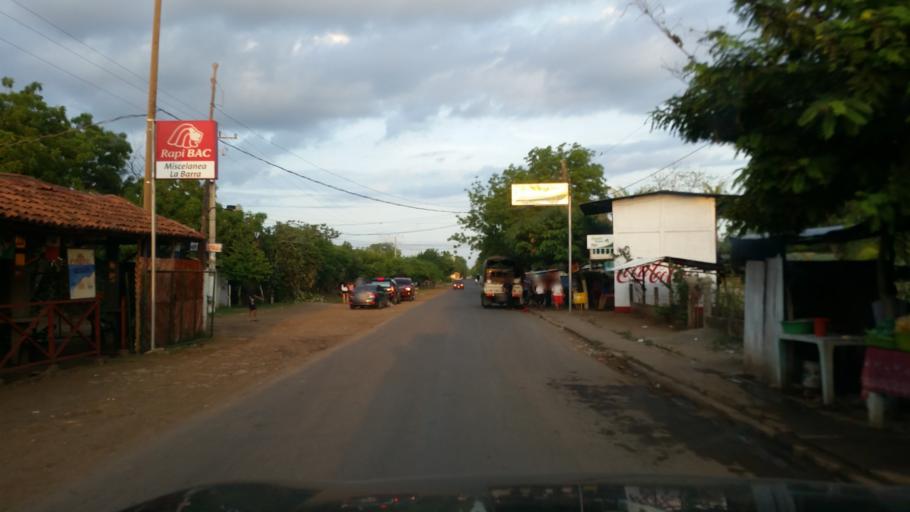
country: NI
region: Managua
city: Masachapa
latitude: 11.7795
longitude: -86.5136
